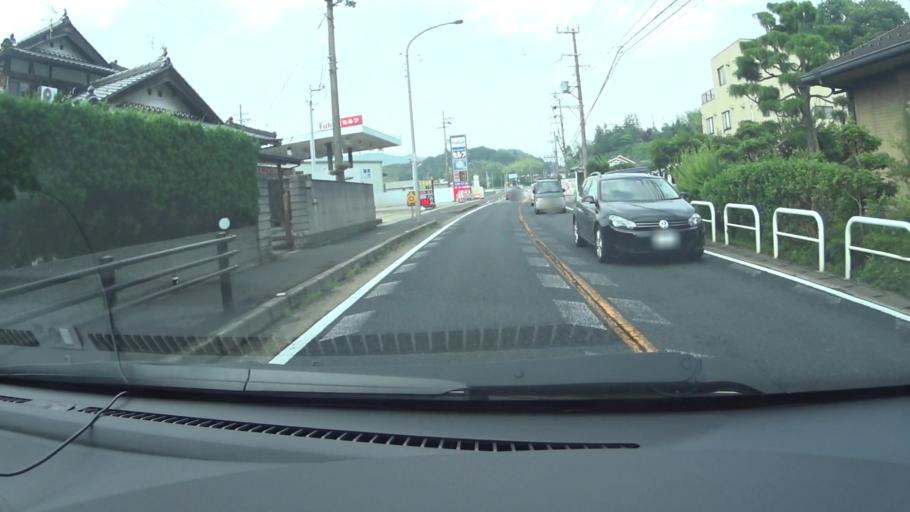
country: JP
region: Kyoto
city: Ayabe
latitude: 35.3256
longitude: 135.2920
